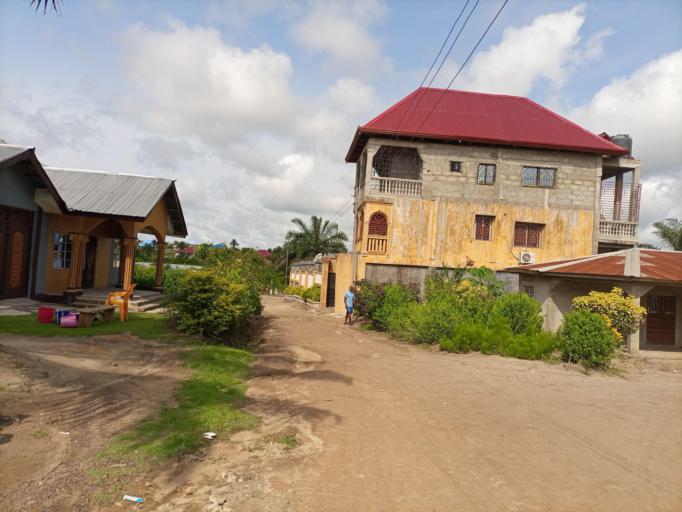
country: SL
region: Southern Province
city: Bo
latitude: 7.9665
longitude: -11.7694
